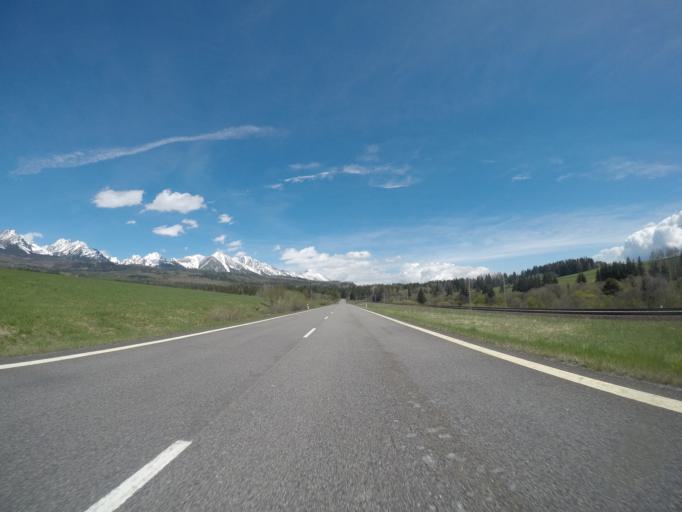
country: SK
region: Presovsky
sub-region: Okres Poprad
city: Strba
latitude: 49.0825
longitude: 20.0506
